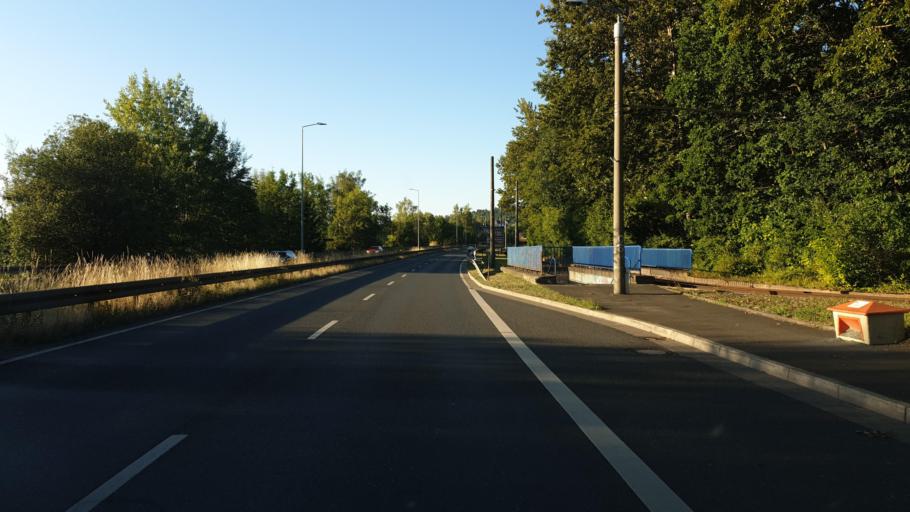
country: DE
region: Saxony
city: Plauen
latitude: 50.5027
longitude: 12.1712
